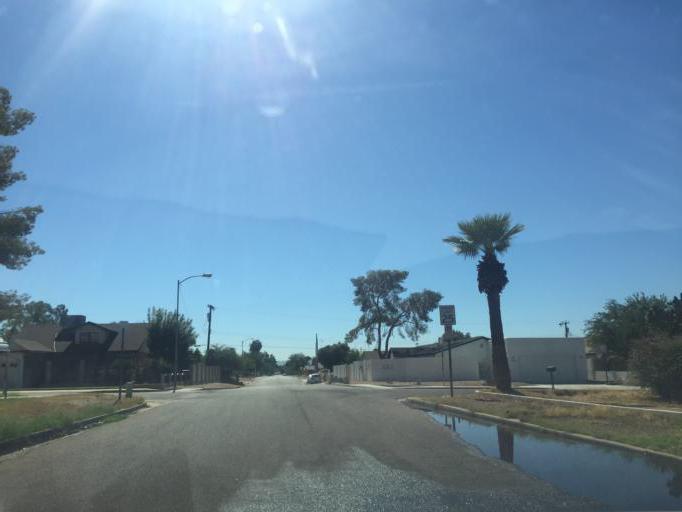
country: US
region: Arizona
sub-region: Maricopa County
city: Phoenix
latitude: 33.5525
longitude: -112.0544
